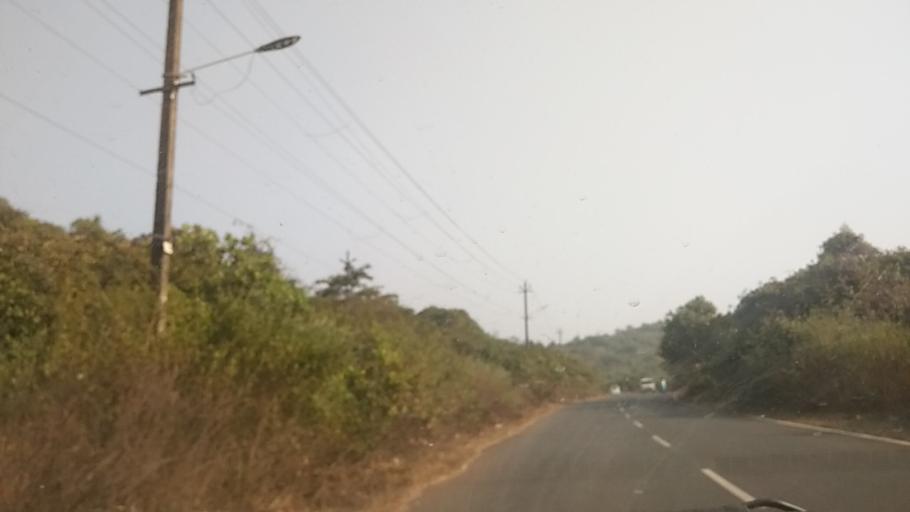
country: IN
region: Goa
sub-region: North Goa
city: Morjim
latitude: 15.6535
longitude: 73.7550
